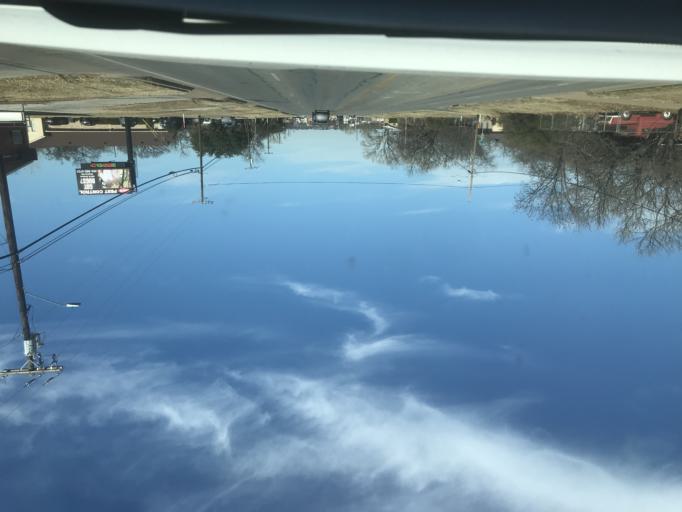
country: US
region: Texas
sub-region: Erath County
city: Stephenville
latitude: 32.2284
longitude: -98.2175
